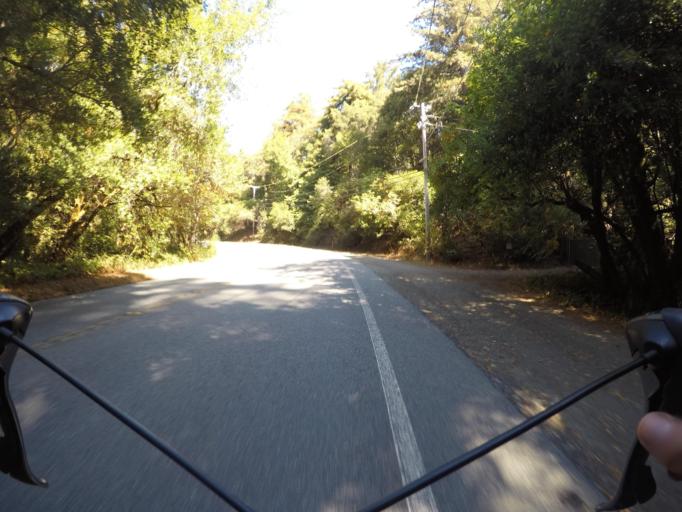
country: US
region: California
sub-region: San Mateo County
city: Portola Valley
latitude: 37.3374
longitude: -122.2692
